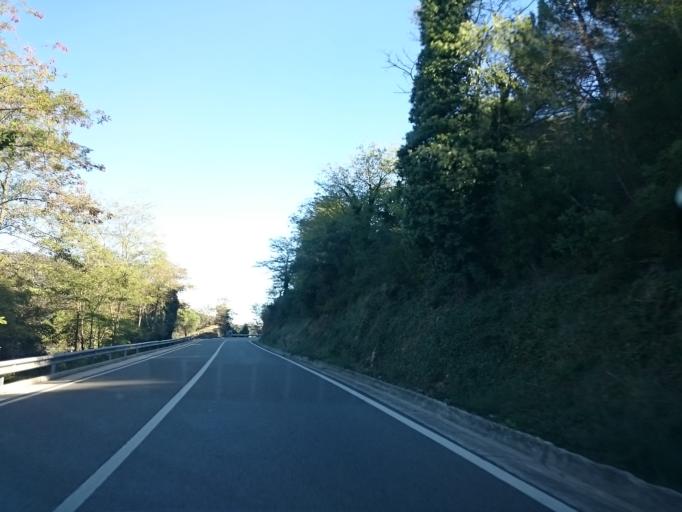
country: ES
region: Catalonia
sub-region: Provincia de Barcelona
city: Capellades
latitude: 41.5349
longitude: 1.6803
